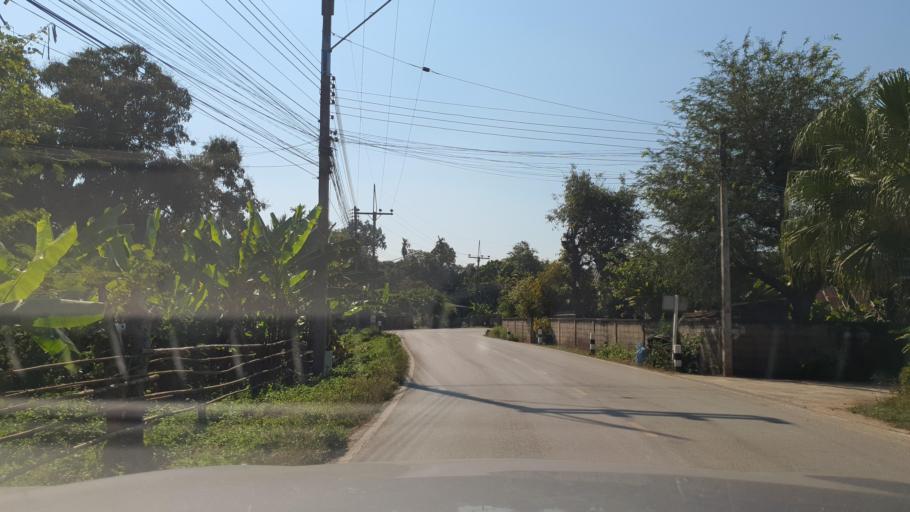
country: TH
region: Chiang Rai
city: Mae Lao
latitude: 19.7641
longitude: 99.7296
